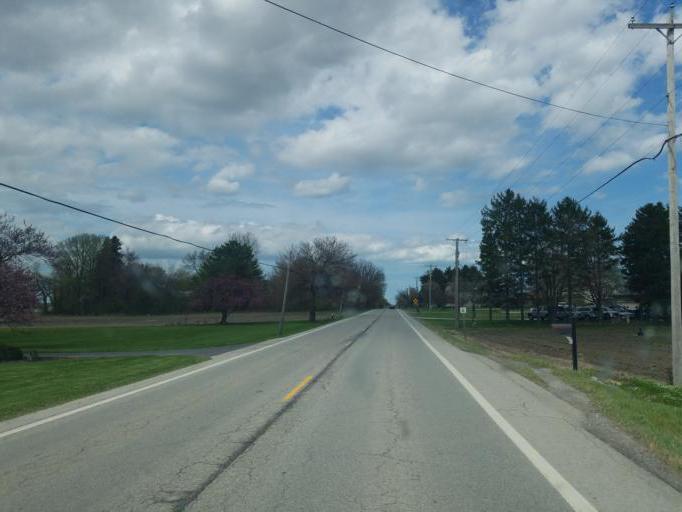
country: US
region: Ohio
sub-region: Erie County
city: Sandusky
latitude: 41.3709
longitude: -82.7448
